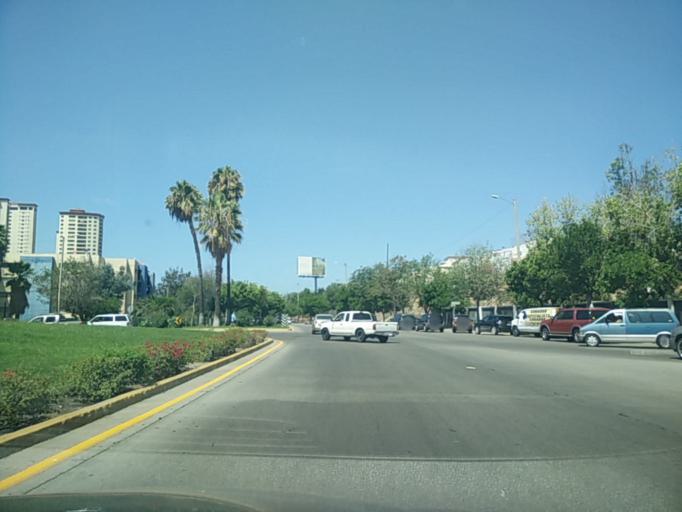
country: MX
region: Baja California
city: Tijuana
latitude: 32.5354
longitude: -117.0170
